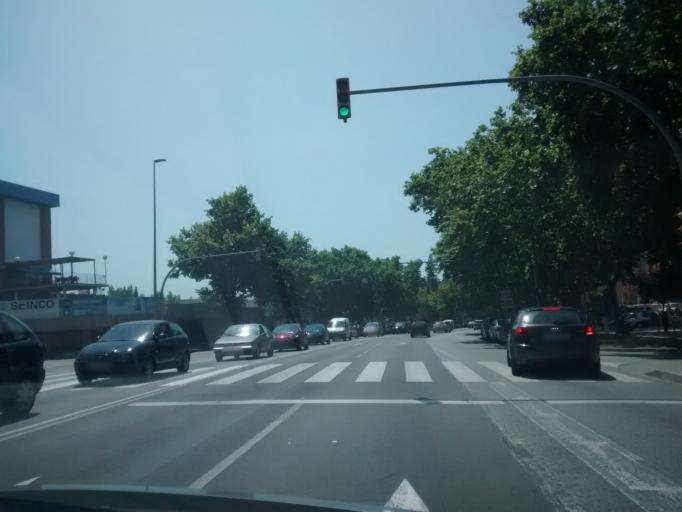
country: ES
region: Catalonia
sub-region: Provincia de Barcelona
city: Sabadell
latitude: 41.5446
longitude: 2.1168
